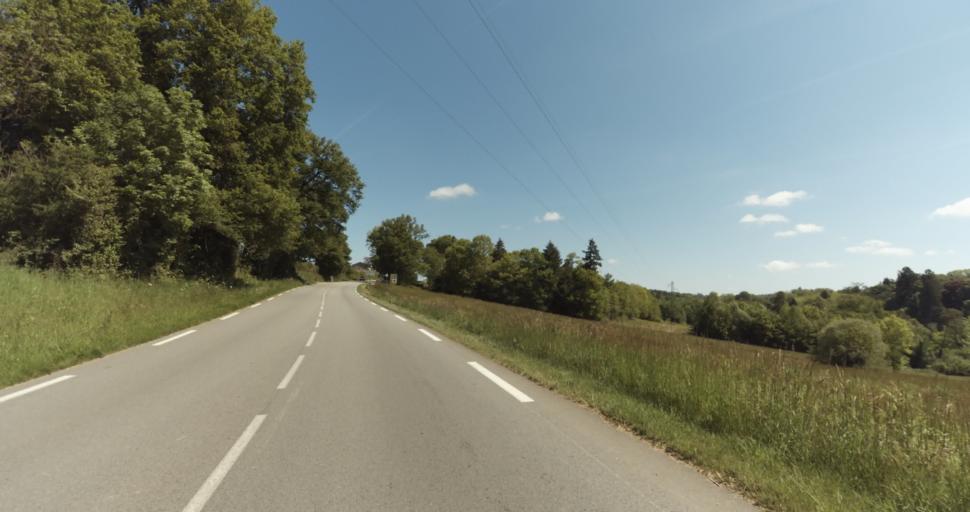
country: FR
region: Limousin
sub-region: Departement de la Haute-Vienne
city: Le Vigen
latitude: 45.7602
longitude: 1.2936
